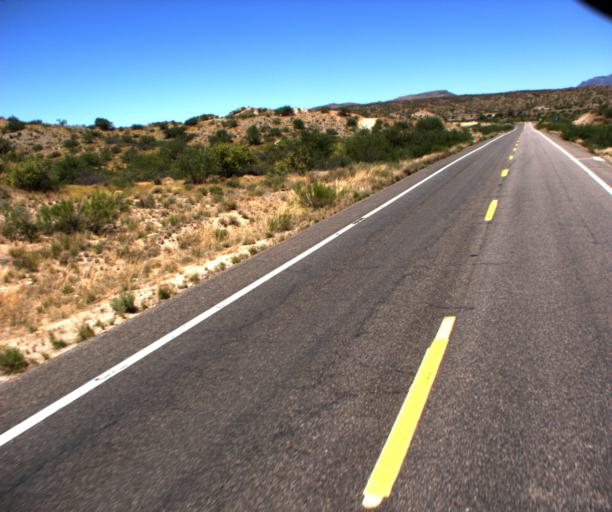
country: US
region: Arizona
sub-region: Gila County
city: Globe
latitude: 33.3683
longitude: -110.7374
